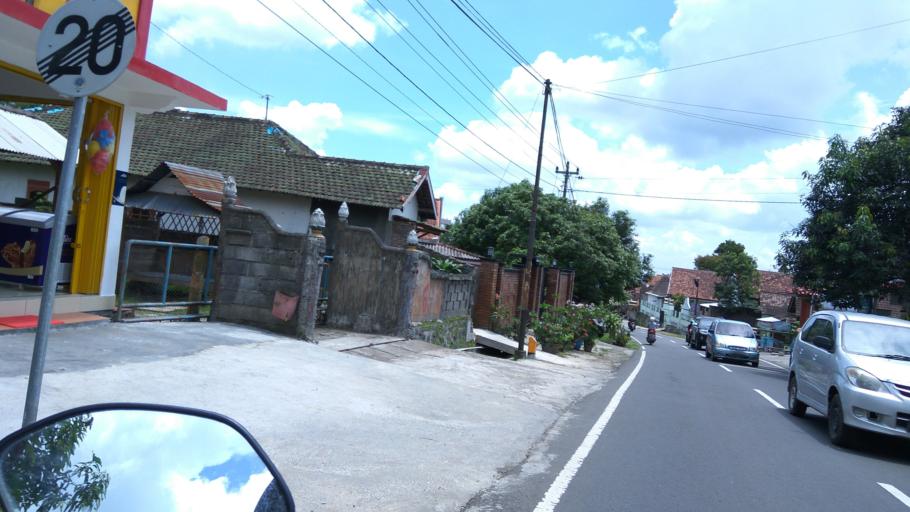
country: ID
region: Central Java
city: Ambarawa
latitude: -7.2446
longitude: 110.3960
